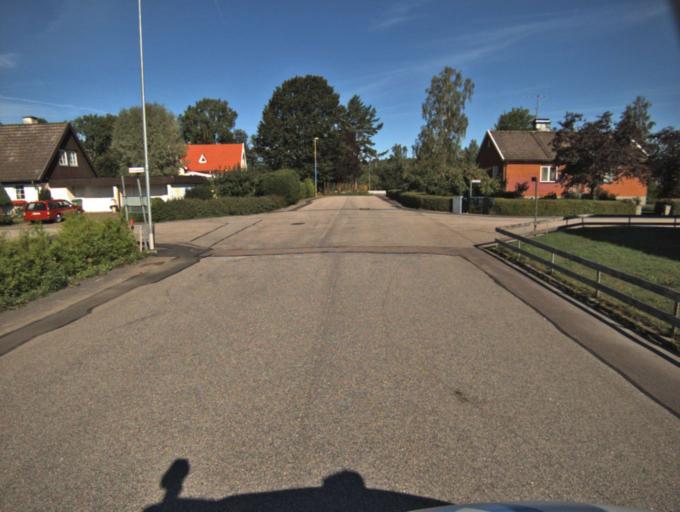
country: SE
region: Vaestra Goetaland
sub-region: Ulricehamns Kommun
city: Ulricehamn
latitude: 57.8969
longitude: 13.4633
